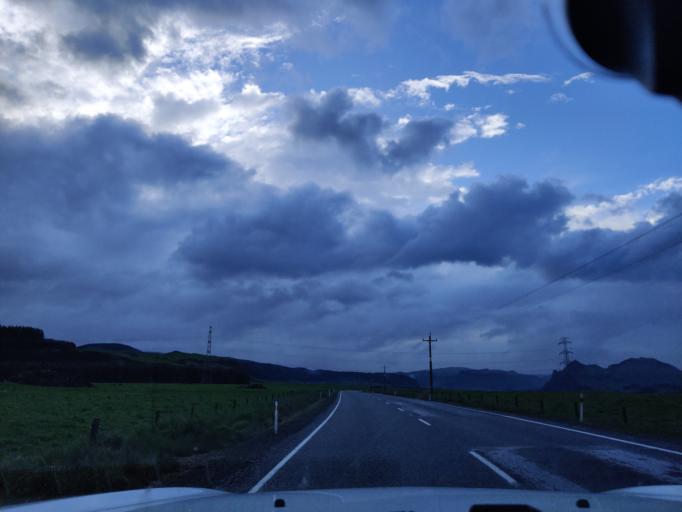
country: NZ
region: Waikato
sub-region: South Waikato District
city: Tokoroa
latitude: -38.3945
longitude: 175.7824
